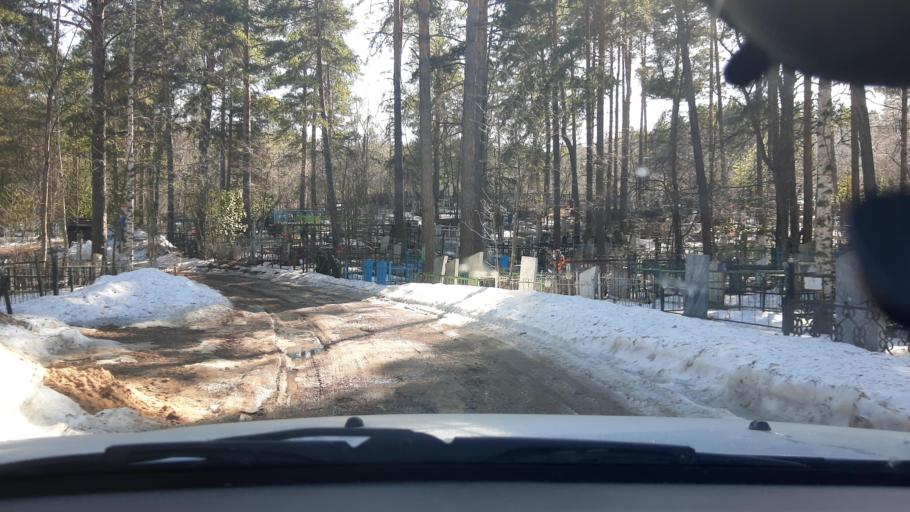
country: RU
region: Nizjnij Novgorod
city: Pyra
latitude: 56.2426
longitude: 43.3673
